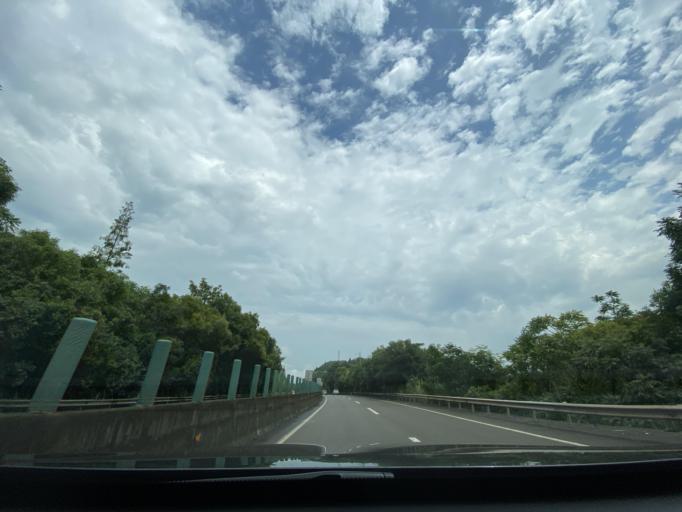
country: CN
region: Sichuan
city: Jiancheng
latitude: 30.2769
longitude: 104.5933
